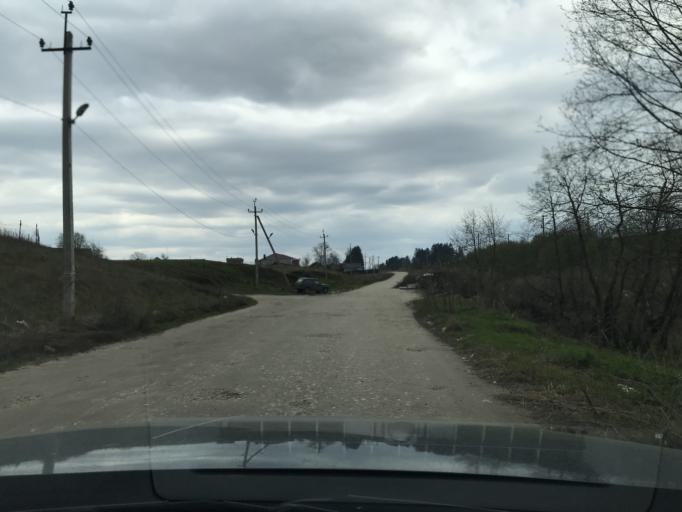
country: RU
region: Vladimir
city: Strunino
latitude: 56.3787
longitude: 38.5939
